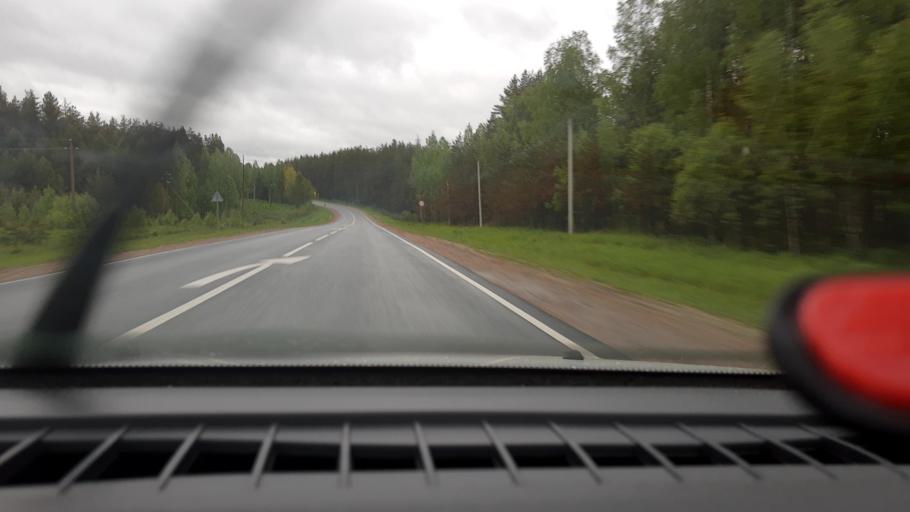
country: RU
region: Nizjnij Novgorod
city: Krasnyye Baki
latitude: 57.0191
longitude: 45.1169
